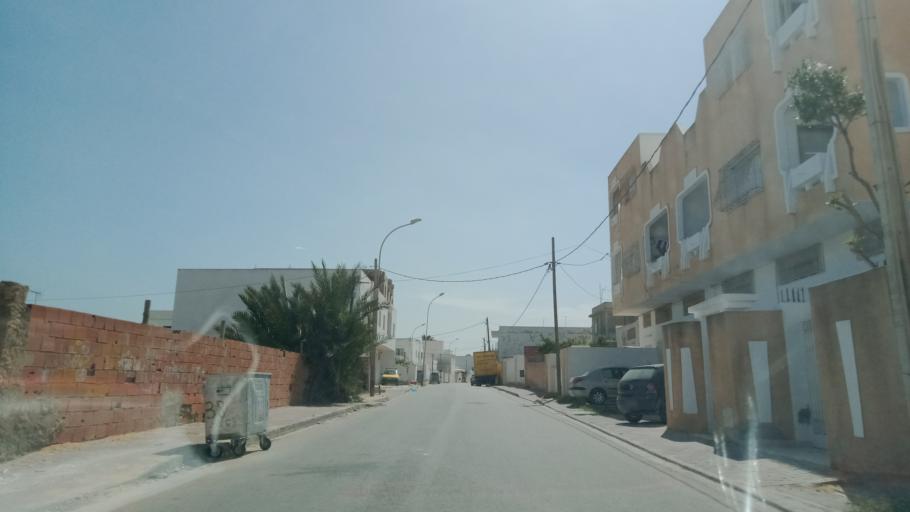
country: TN
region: Safaqis
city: Al Qarmadah
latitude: 34.8036
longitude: 10.7583
